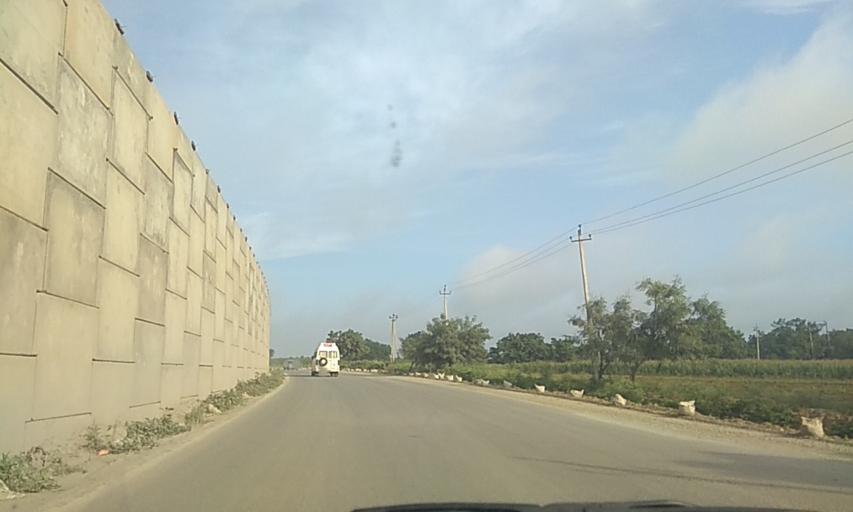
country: IN
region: Karnataka
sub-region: Haveri
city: Haveri
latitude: 14.7599
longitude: 75.4398
